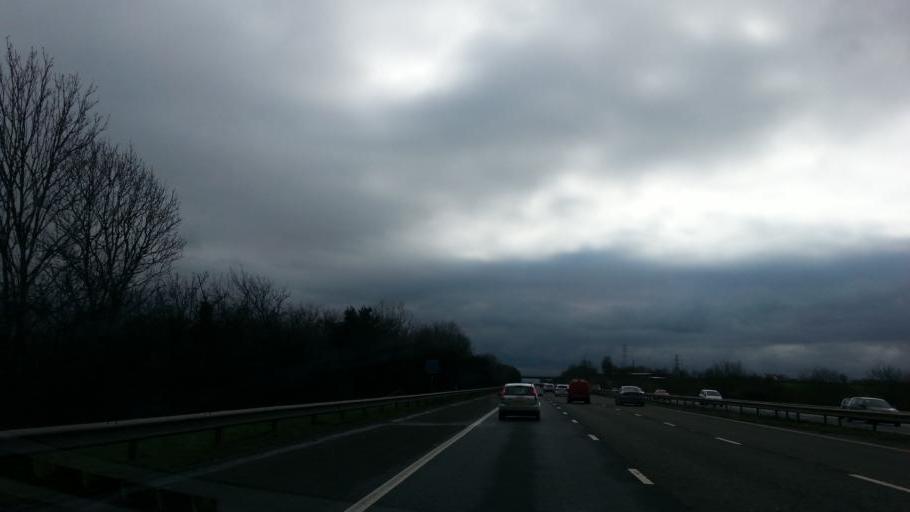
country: GB
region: England
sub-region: Somerset
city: North Petherton
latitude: 51.0741
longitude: -3.0119
